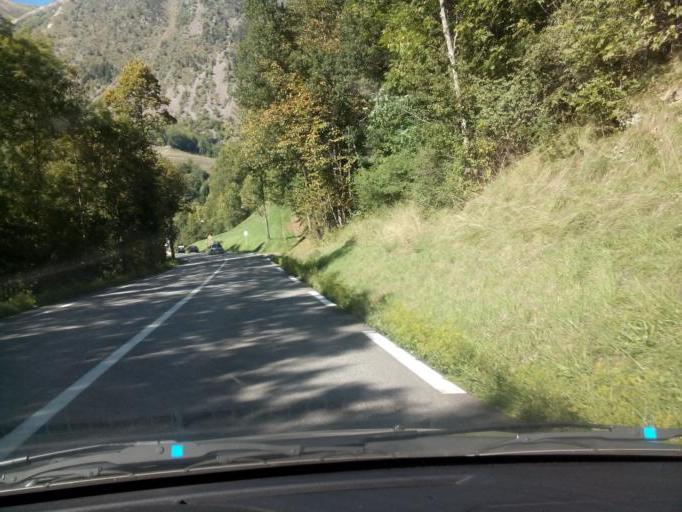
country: FR
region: Rhone-Alpes
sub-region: Departement de l'Isere
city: Mont-de-Lans
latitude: 45.0429
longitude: 6.1271
